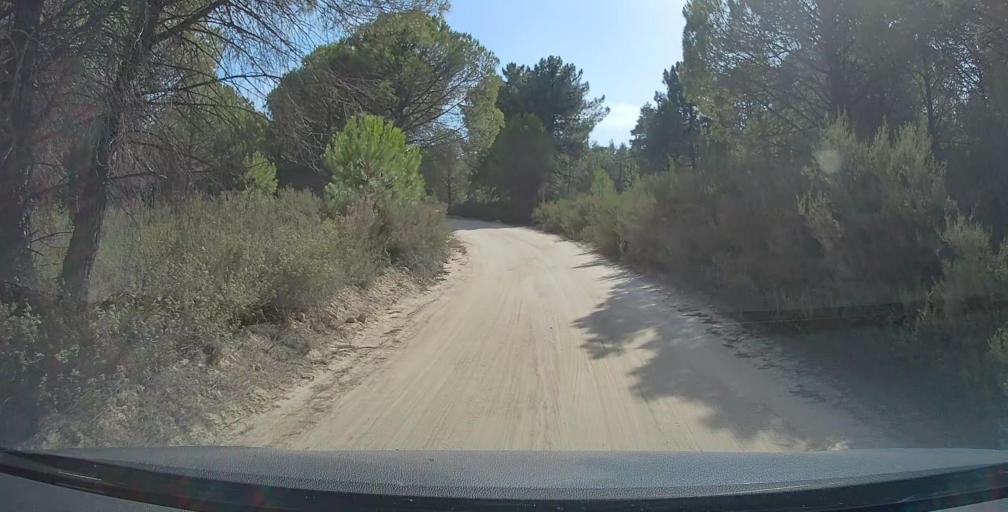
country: GR
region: Central Macedonia
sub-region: Nomos Chalkidikis
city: Sarti
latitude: 40.1277
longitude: 23.9514
